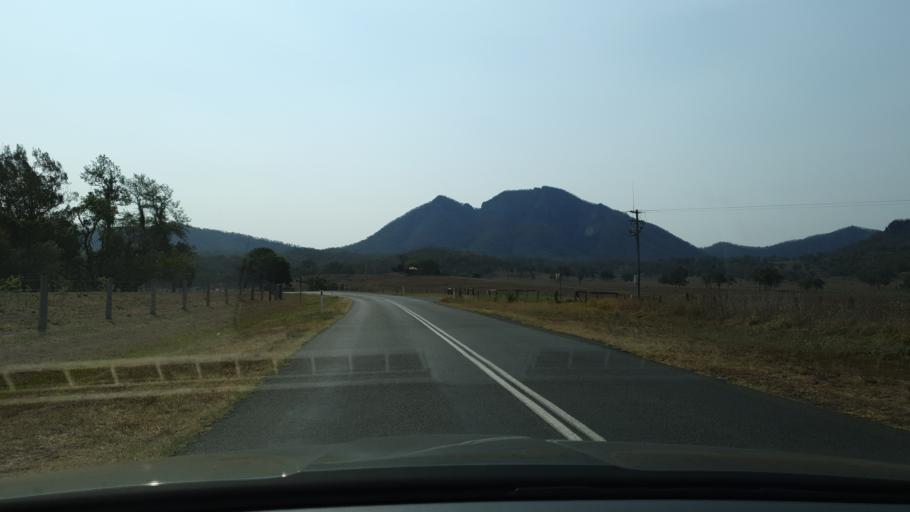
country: AU
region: Queensland
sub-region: Ipswich
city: Deebing Heights
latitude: -28.1373
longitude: 152.5840
